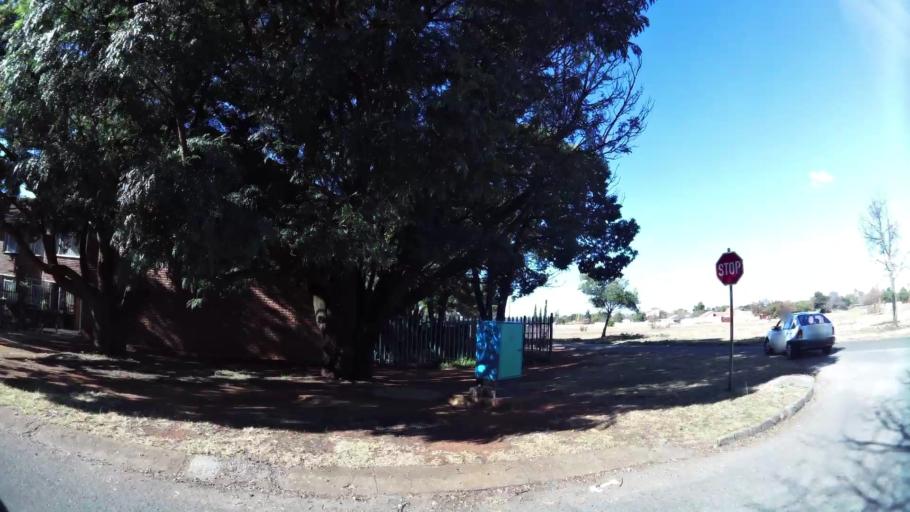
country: ZA
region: Gauteng
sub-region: West Rand District Municipality
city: Carletonville
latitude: -26.3623
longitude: 27.3666
